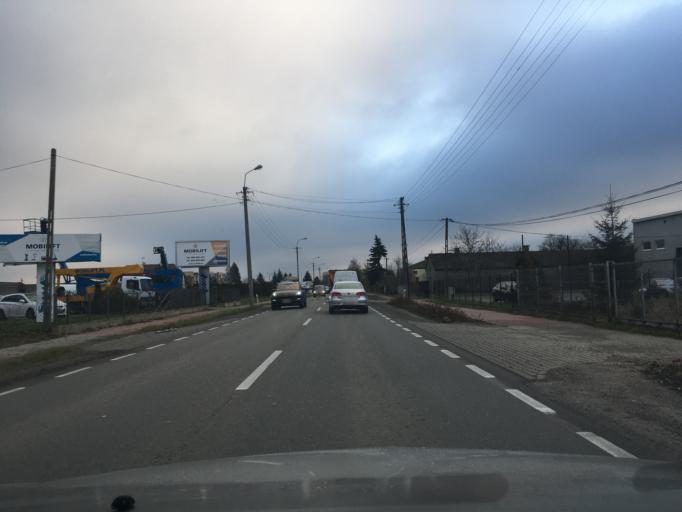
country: PL
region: Masovian Voivodeship
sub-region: Powiat piaseczynski
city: Lesznowola
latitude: 52.0847
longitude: 20.9537
